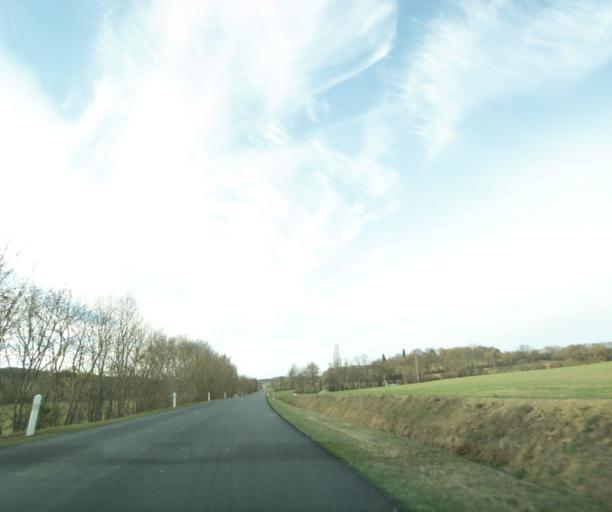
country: FR
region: Midi-Pyrenees
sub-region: Departement du Gers
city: Jegun
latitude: 43.6825
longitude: 0.4946
